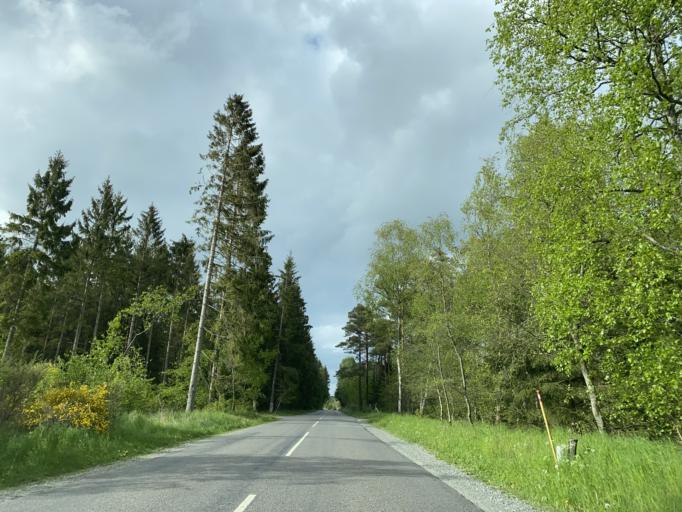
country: DK
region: Central Jutland
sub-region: Skanderborg Kommune
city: Ry
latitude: 56.0617
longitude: 9.6920
